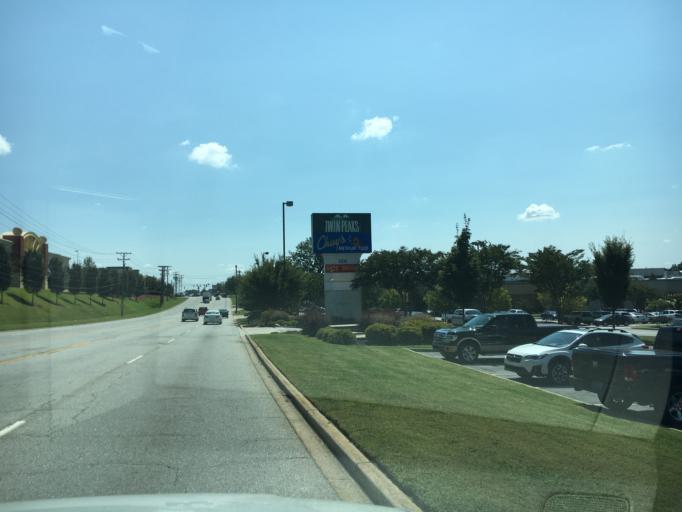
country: US
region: South Carolina
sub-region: Greenville County
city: Mauldin
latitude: 34.8348
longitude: -82.3110
